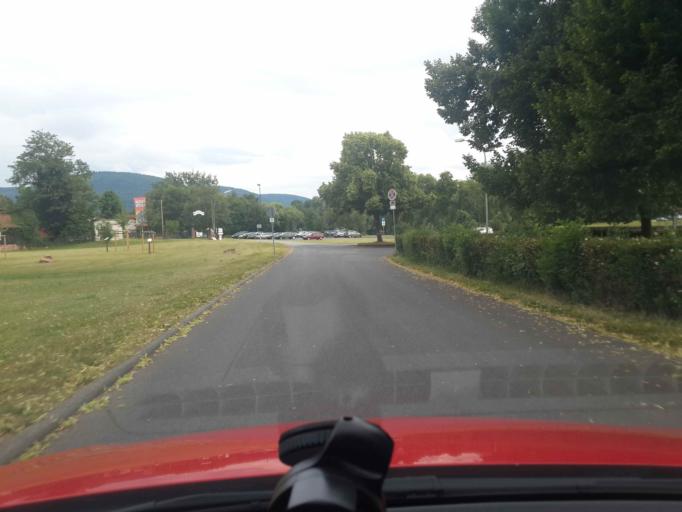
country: DE
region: Bavaria
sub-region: Regierungsbezirk Unterfranken
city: Grossheubach
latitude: 49.7245
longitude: 9.2206
